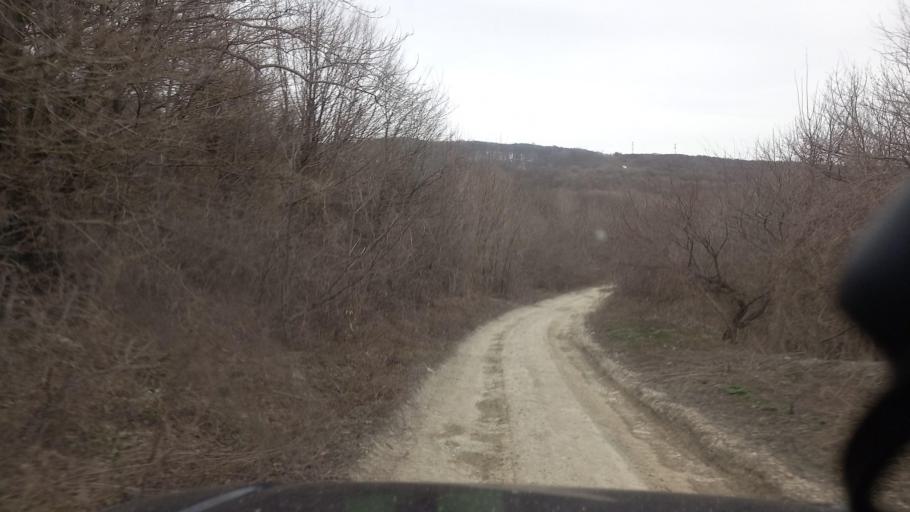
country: RU
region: Krasnodarskiy
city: Pshada
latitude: 44.5961
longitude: 38.2927
